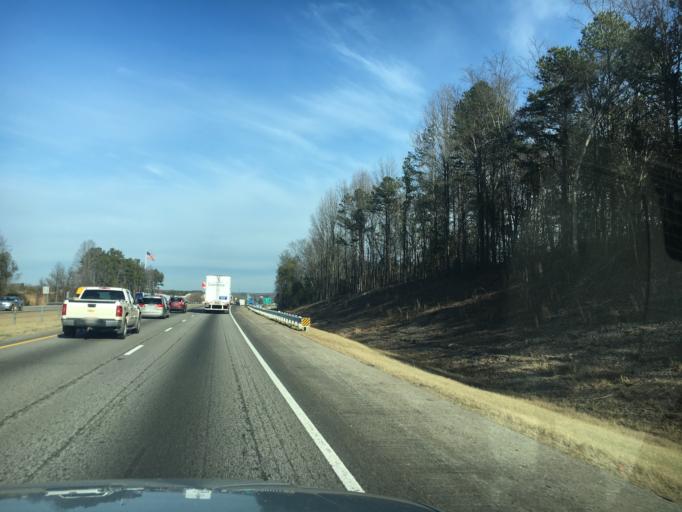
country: US
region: Georgia
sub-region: Jackson County
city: Commerce
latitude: 34.2459
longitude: -83.4784
